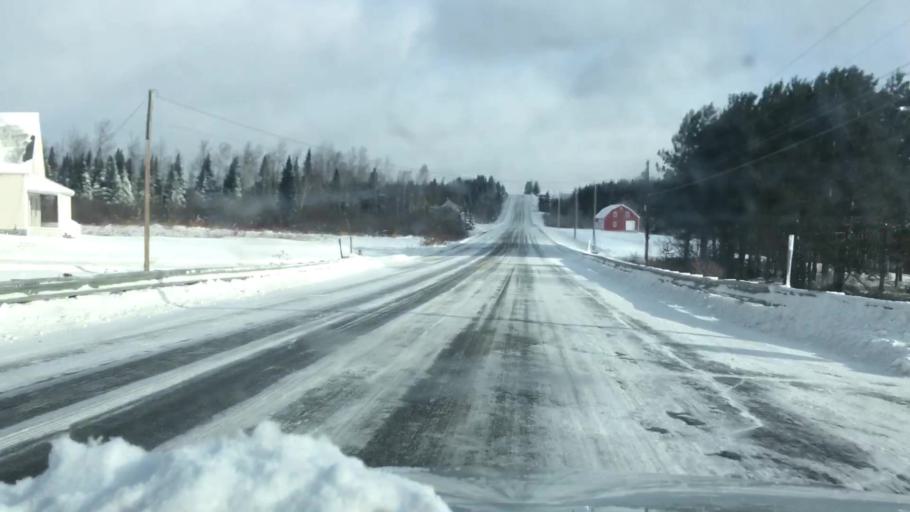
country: US
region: Maine
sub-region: Aroostook County
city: Van Buren
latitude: 47.0915
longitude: -67.9814
